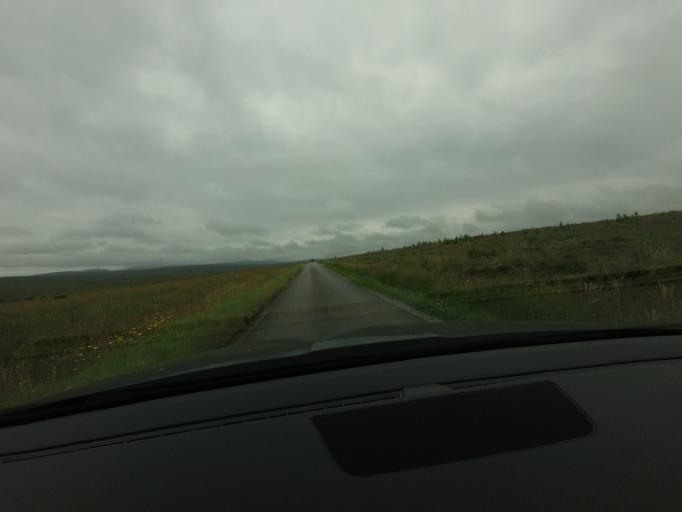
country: GB
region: Scotland
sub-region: Highland
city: Evanton
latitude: 58.1767
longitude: -4.5141
